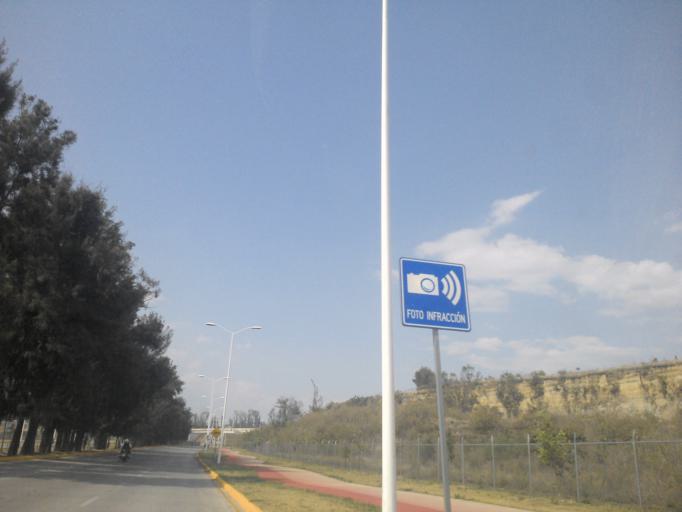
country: MX
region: Jalisco
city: Zapopan2
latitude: 20.6851
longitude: -103.4599
